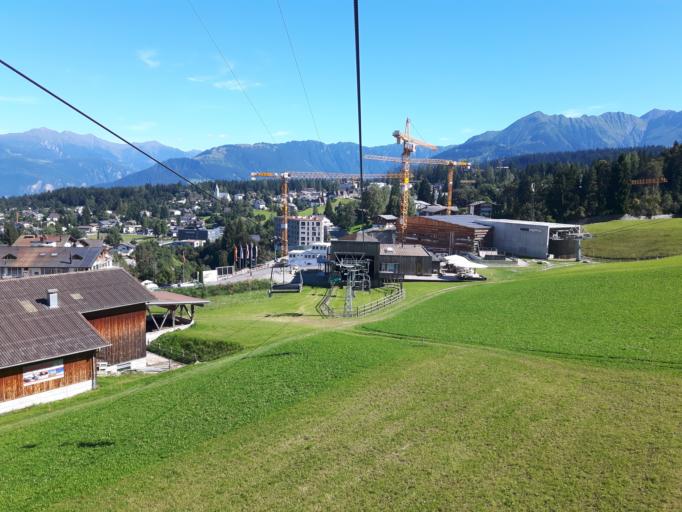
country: CH
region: Grisons
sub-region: Imboden District
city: Flims
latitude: 46.8350
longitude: 9.2802
